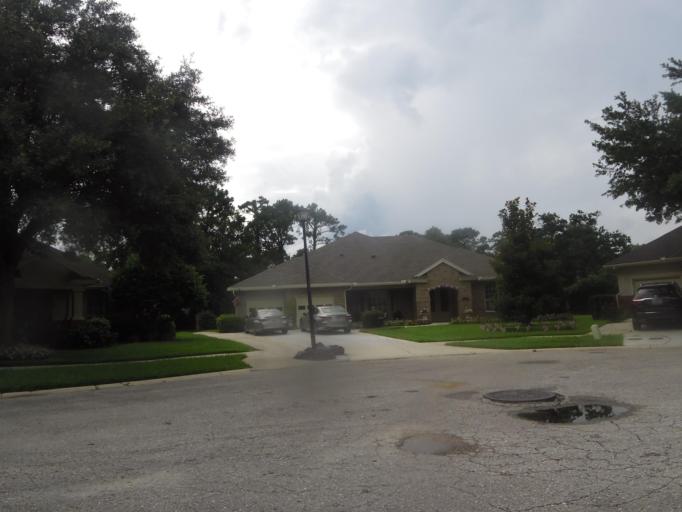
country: US
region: Florida
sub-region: Duval County
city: Jacksonville Beach
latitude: 30.2630
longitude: -81.4578
